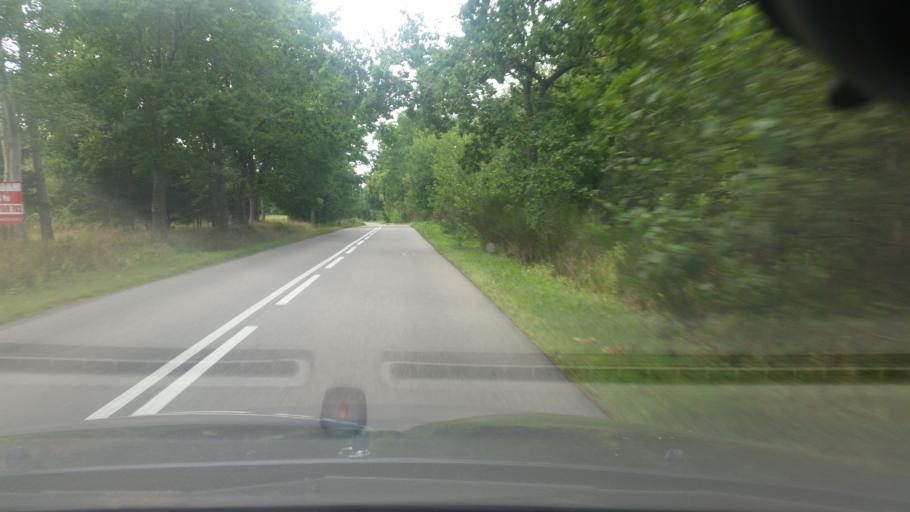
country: PL
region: Pomeranian Voivodeship
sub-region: Powiat leborski
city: Leba
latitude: 54.7442
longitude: 17.6553
